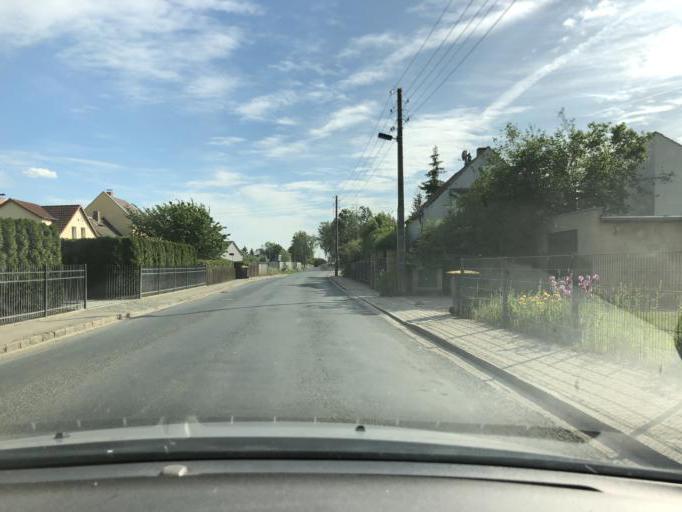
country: DE
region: Saxony
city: Borsdorf
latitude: 51.3227
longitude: 12.5257
